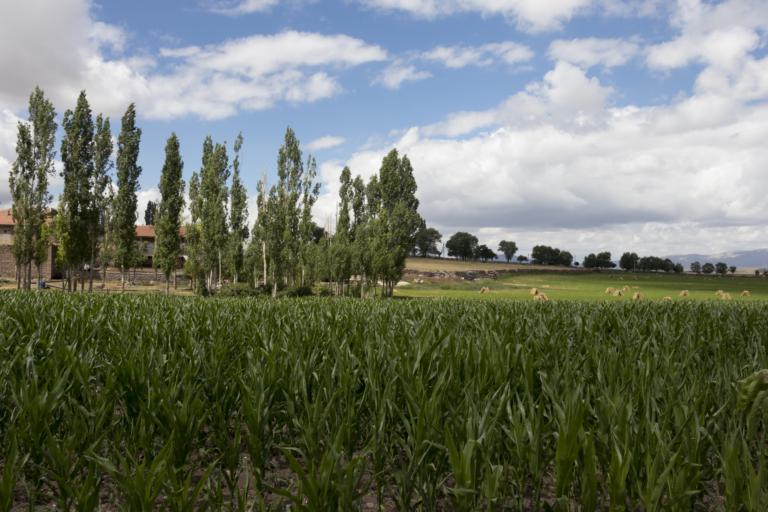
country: TR
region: Kayseri
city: Toklar
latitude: 38.4237
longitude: 36.0966
